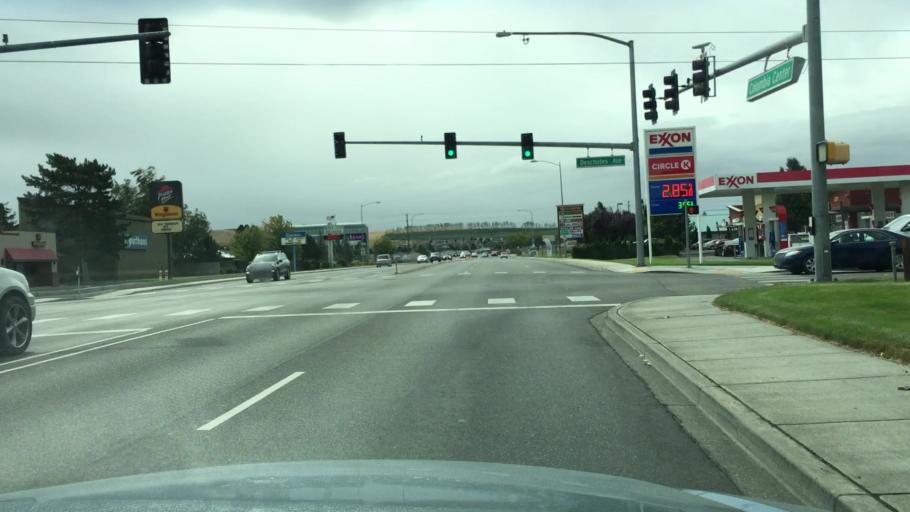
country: US
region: Washington
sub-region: Franklin County
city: West Pasco
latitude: 46.2128
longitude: -119.2257
